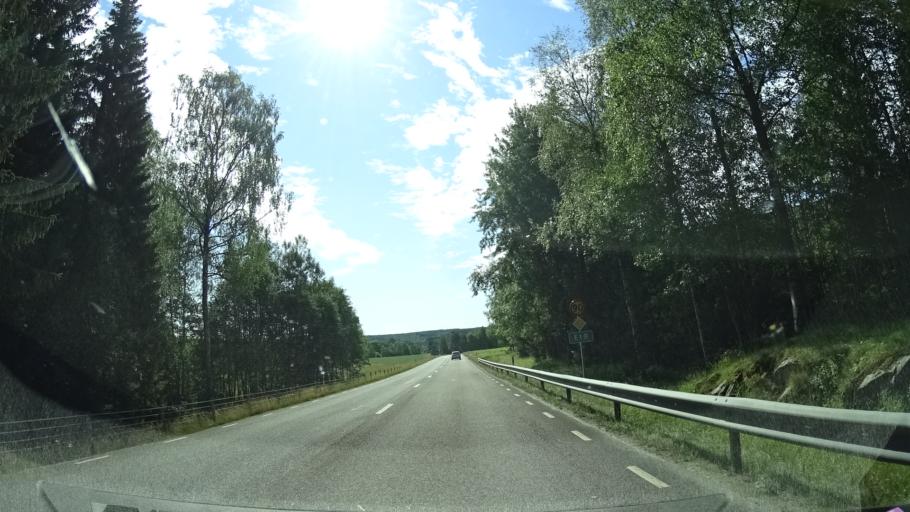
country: SE
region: Vaermland
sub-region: Arjangs Kommun
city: Toecksfors
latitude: 59.4717
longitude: 11.9857
